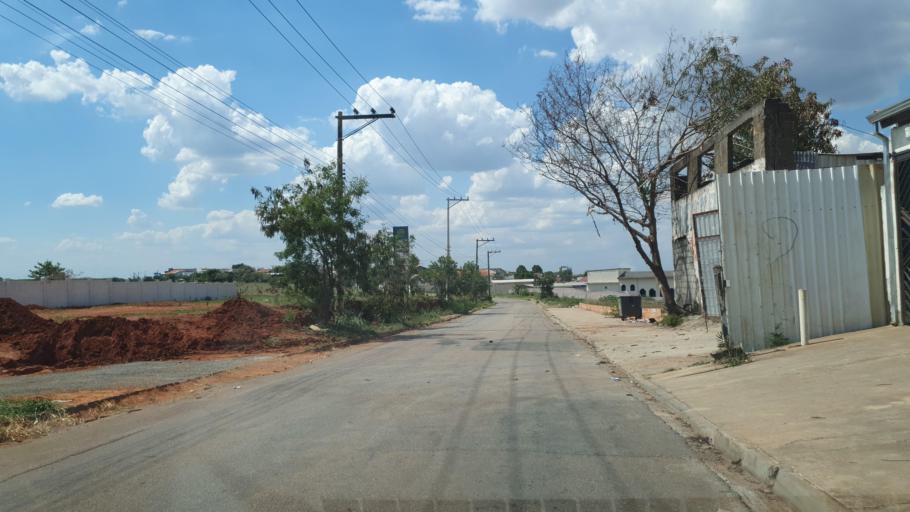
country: BR
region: Sao Paulo
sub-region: Sorocaba
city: Sorocaba
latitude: -23.5054
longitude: -47.5228
